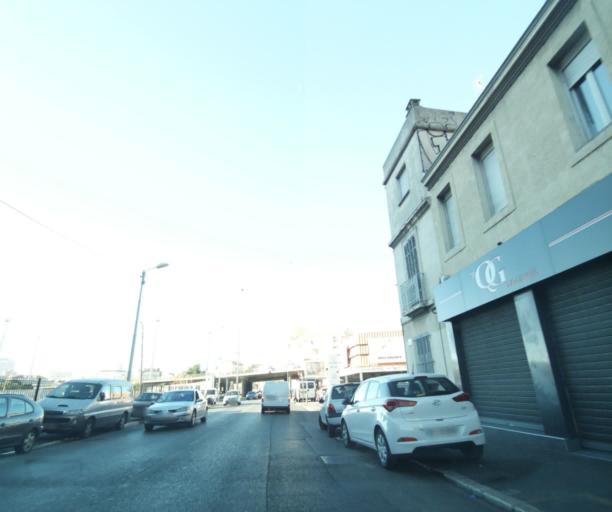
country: FR
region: Provence-Alpes-Cote d'Azur
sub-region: Departement des Bouches-du-Rhone
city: Marseille 05
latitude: 43.2829
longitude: 5.4021
